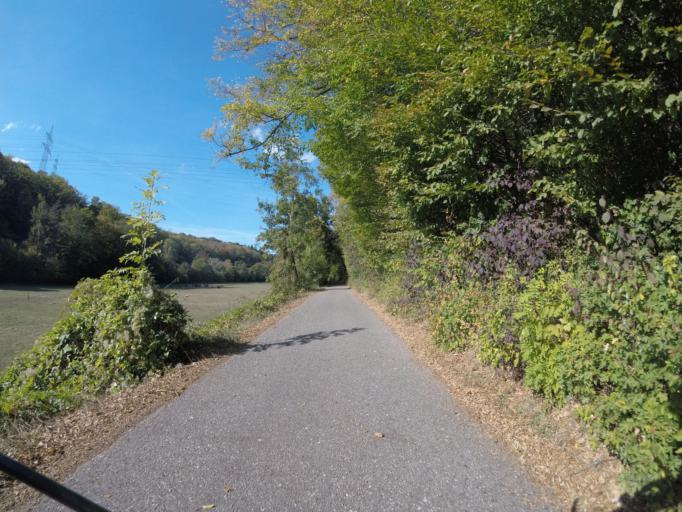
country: DE
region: Baden-Wuerttemberg
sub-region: Karlsruhe Region
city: Olbronn-Durrn
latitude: 48.9962
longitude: 8.7416
